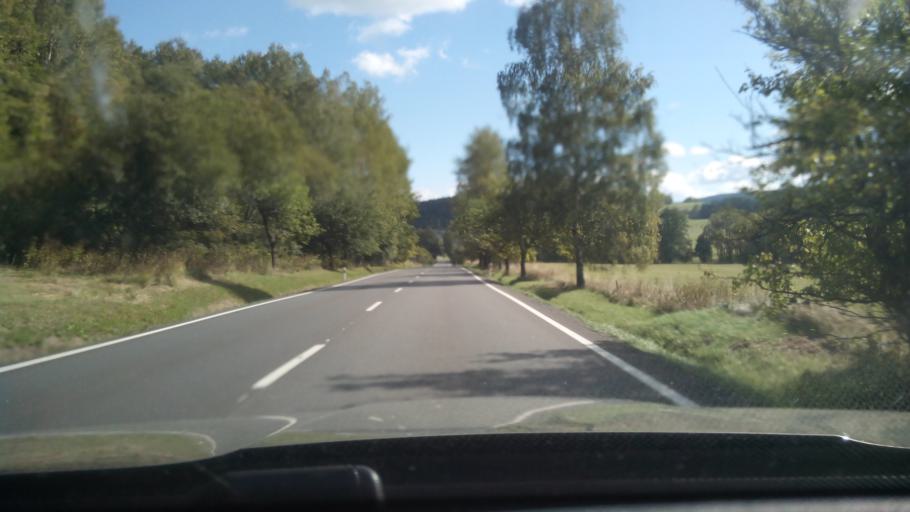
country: CZ
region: Jihocesky
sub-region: Okres Prachatice
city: Stachy
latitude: 49.1011
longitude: 13.6720
